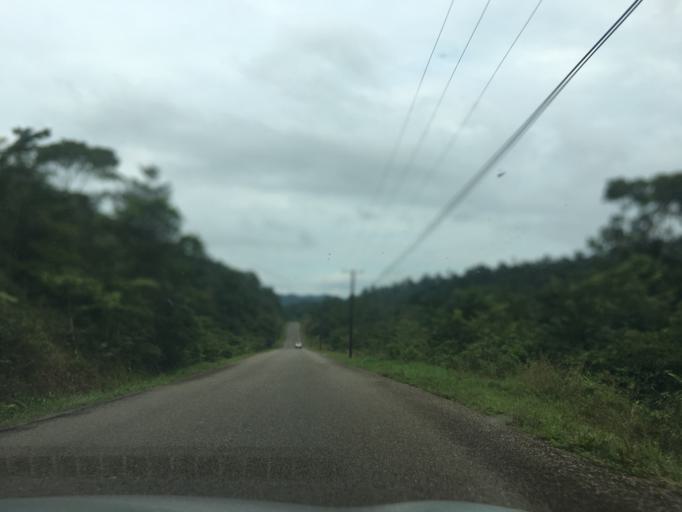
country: BZ
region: Cayo
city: Belmopan
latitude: 17.0808
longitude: -88.5998
